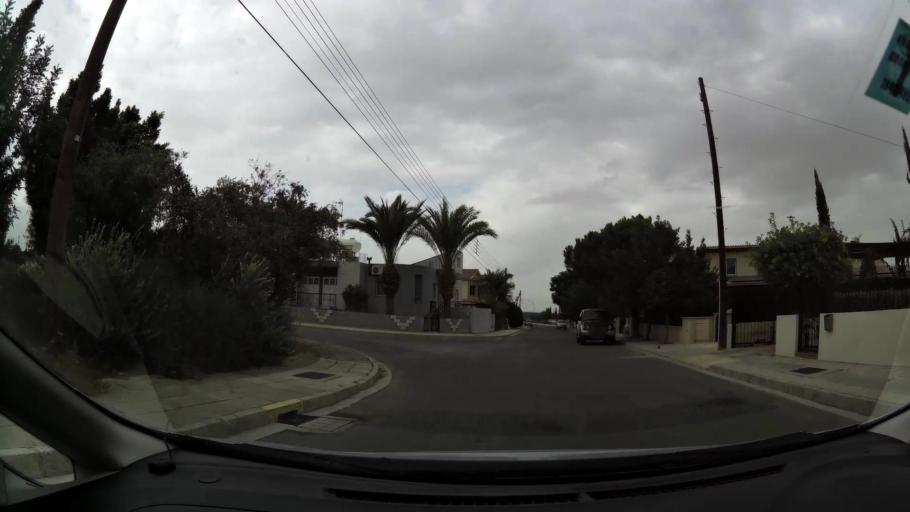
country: CY
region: Lefkosia
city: Geri
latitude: 35.1133
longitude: 33.3923
